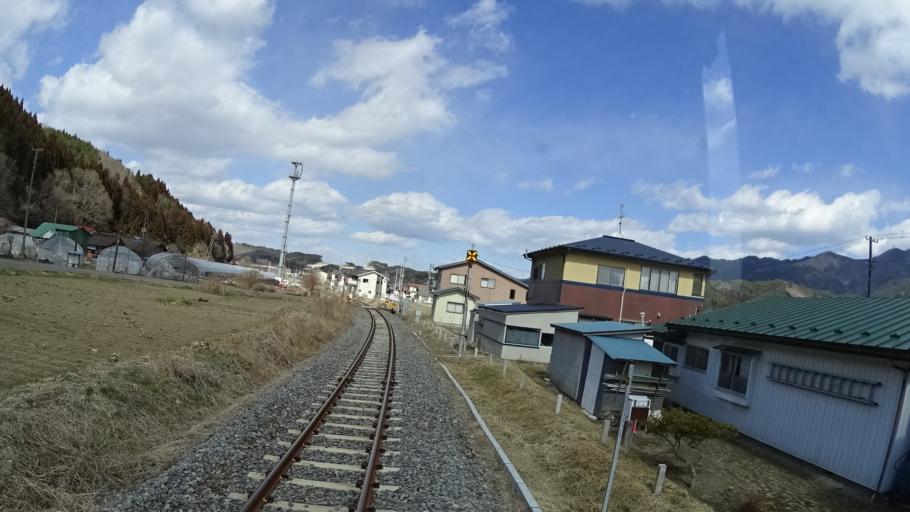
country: JP
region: Iwate
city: Yamada
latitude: 39.5312
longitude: 141.9238
